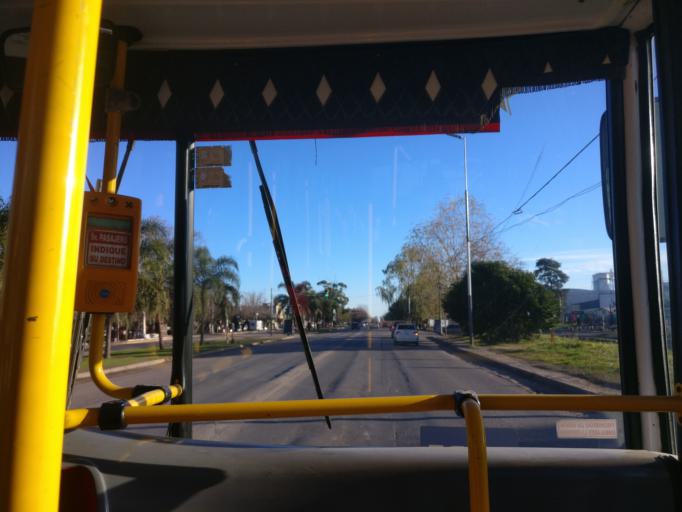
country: AR
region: Buenos Aires
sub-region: Partido de Ezeiza
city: Ezeiza
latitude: -34.9094
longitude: -58.5930
